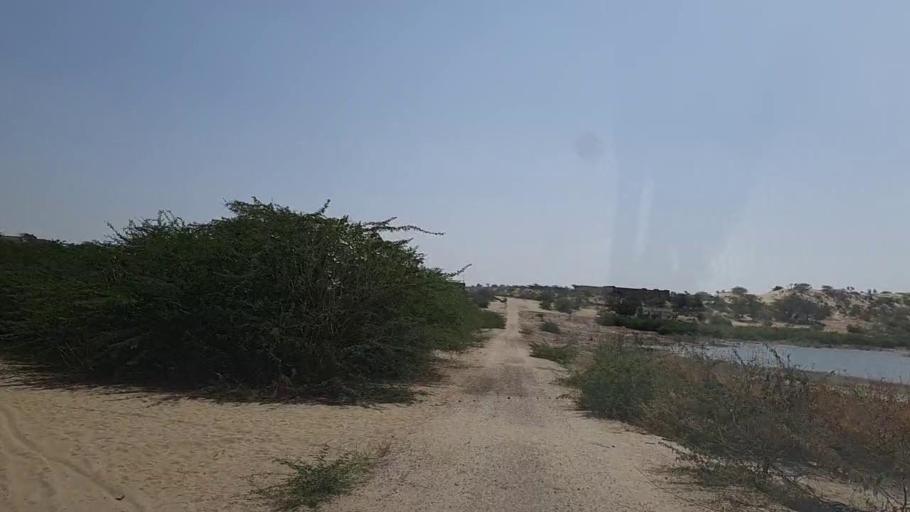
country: PK
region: Sindh
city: Diplo
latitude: 24.5124
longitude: 69.4138
